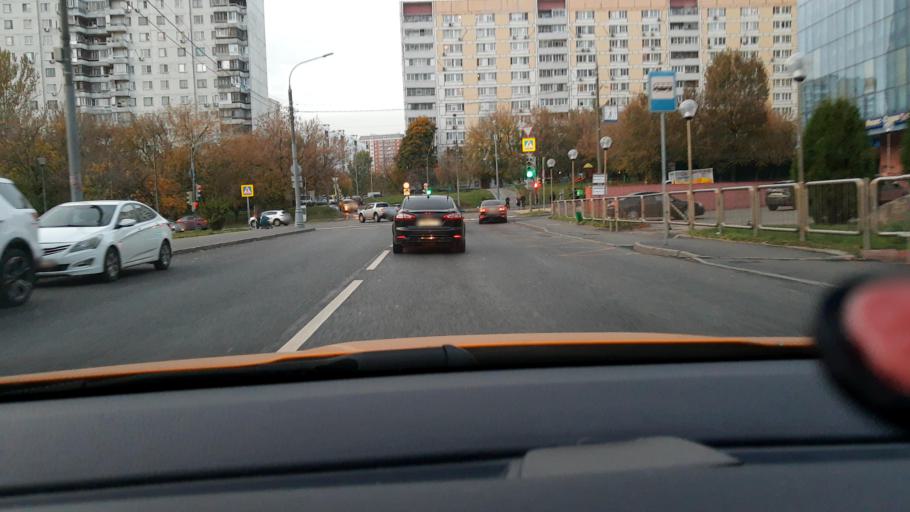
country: RU
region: Moscow
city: Kozeyevo
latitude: 55.8693
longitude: 37.6298
